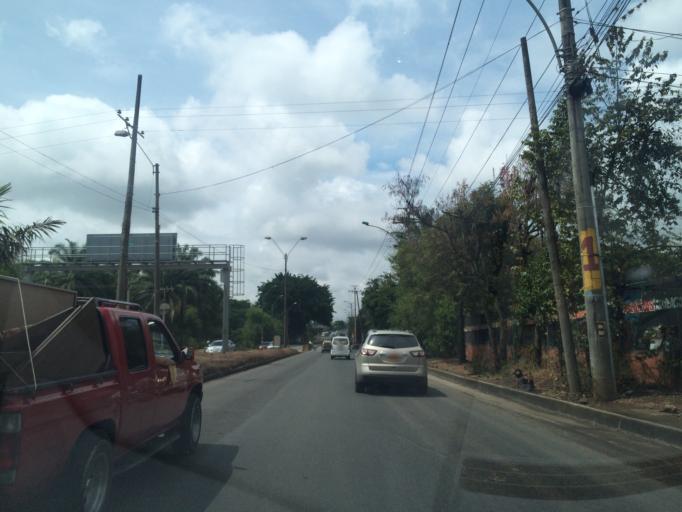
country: CO
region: Valle del Cauca
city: Cali
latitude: 3.3633
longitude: -76.5245
